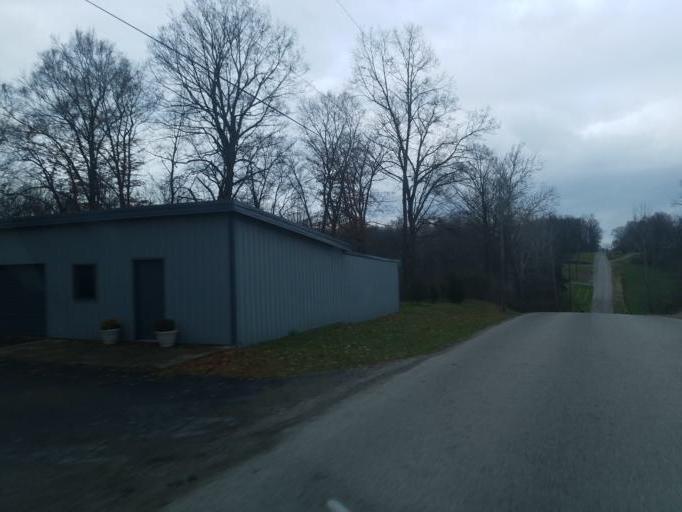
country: US
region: Ohio
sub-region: Morrow County
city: Mount Gilead
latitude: 40.5495
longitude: -82.7966
